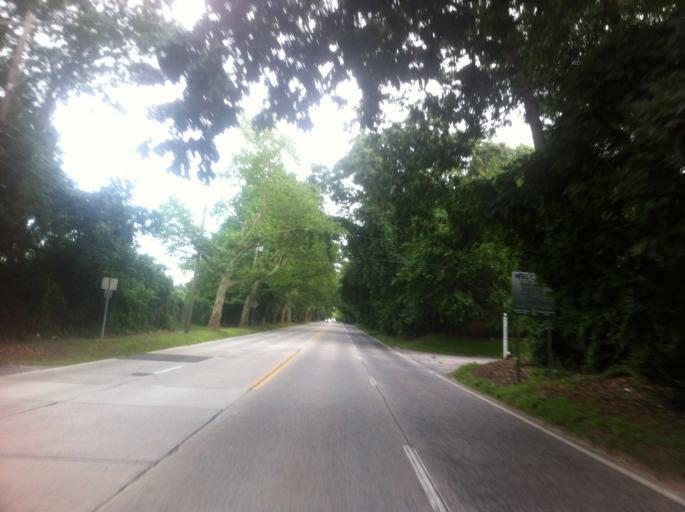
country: US
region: New York
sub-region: Nassau County
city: Lattingtown
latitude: 40.9071
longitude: -73.5840
